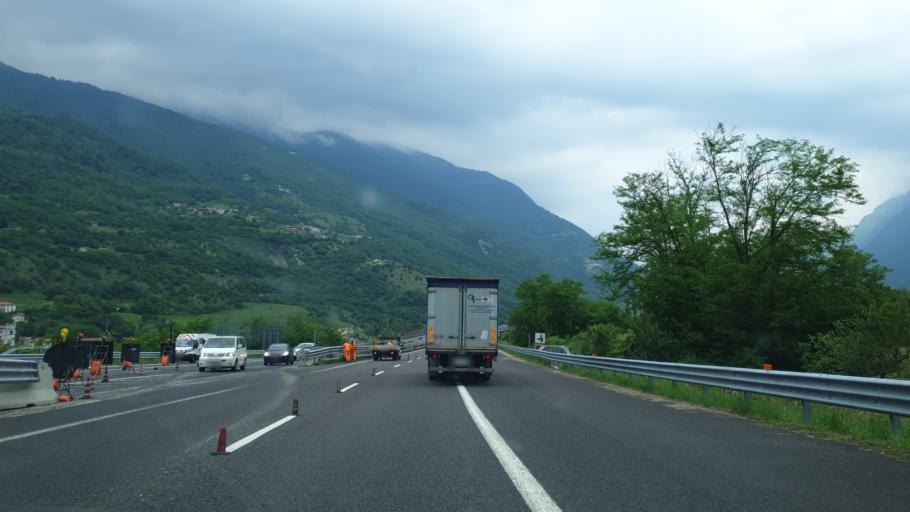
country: IT
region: Veneto
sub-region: Provincia di Treviso
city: Revine
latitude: 46.0021
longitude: 12.2747
